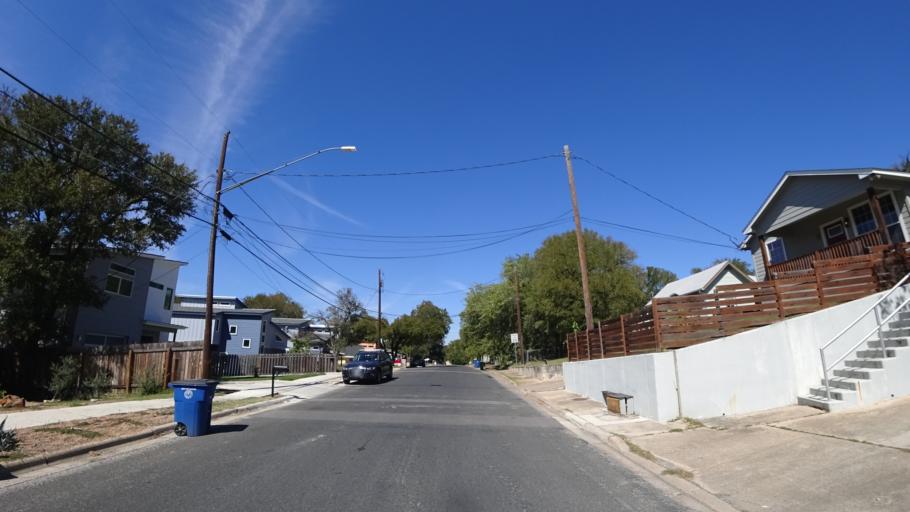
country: US
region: Texas
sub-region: Travis County
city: Austin
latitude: 30.2764
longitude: -97.6791
